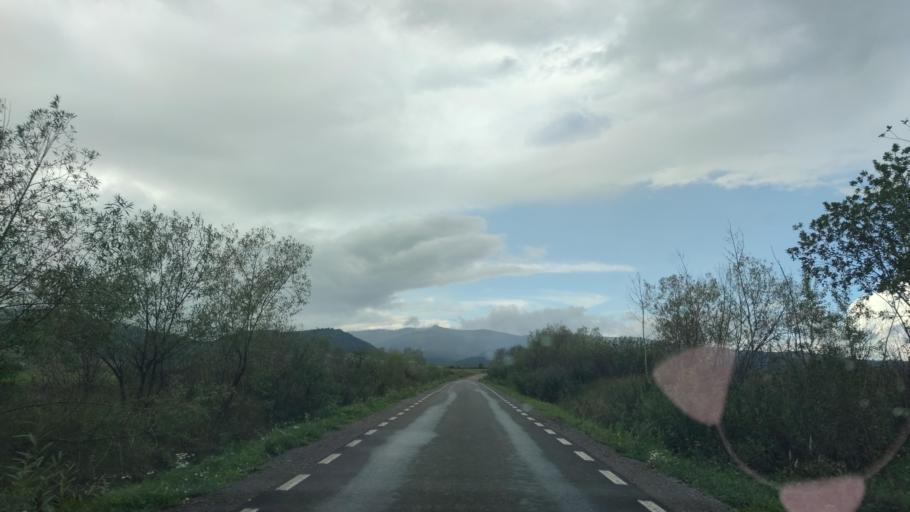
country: RO
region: Harghita
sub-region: Comuna Remetea
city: Remetea
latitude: 46.8078
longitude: 25.4098
